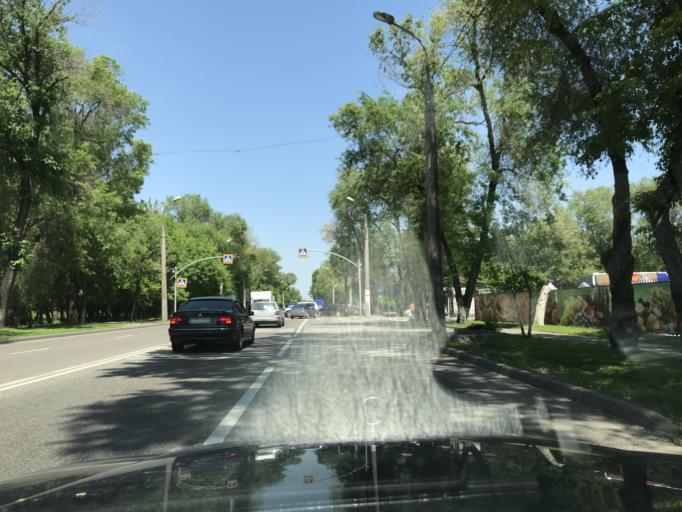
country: KZ
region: Almaty Oblysy
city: Pervomayskiy
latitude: 43.3256
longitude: 76.9593
